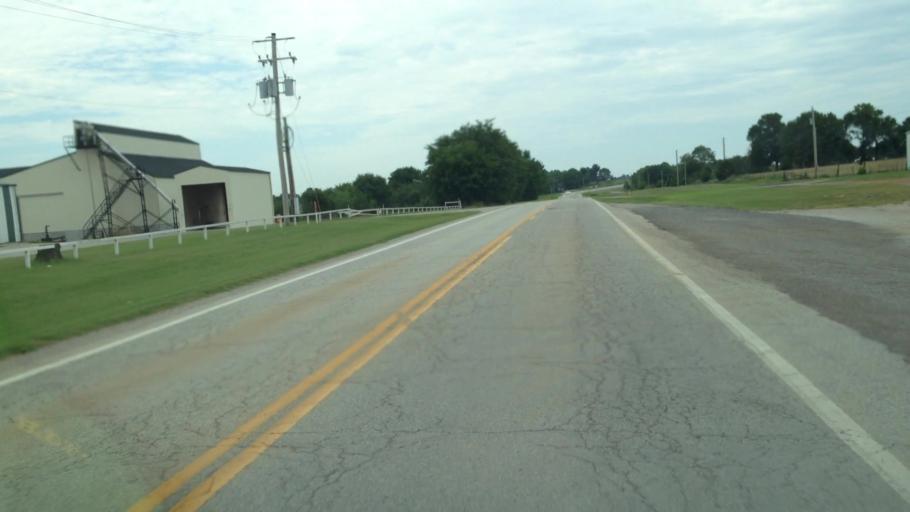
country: US
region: Kansas
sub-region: Labette County
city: Chetopa
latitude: 36.8798
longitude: -95.0989
